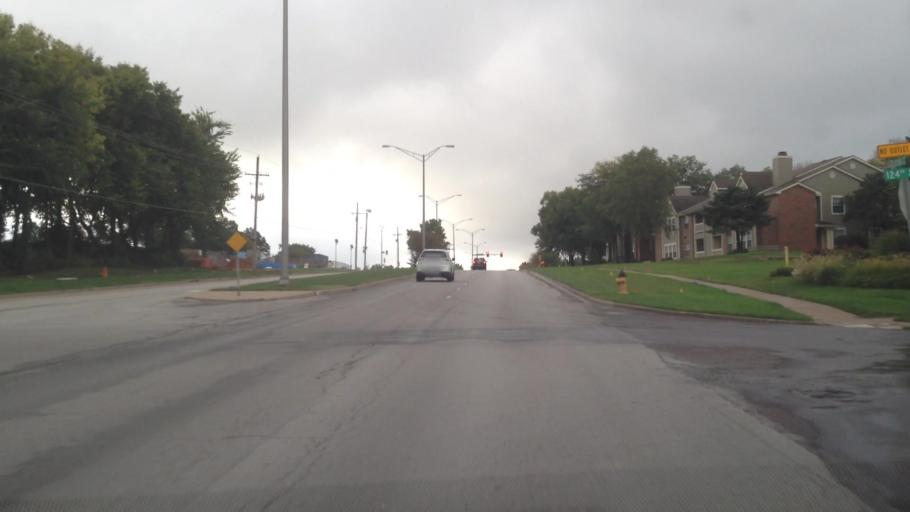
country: US
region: Kansas
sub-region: Johnson County
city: Lenexa
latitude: 38.9035
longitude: -94.7239
